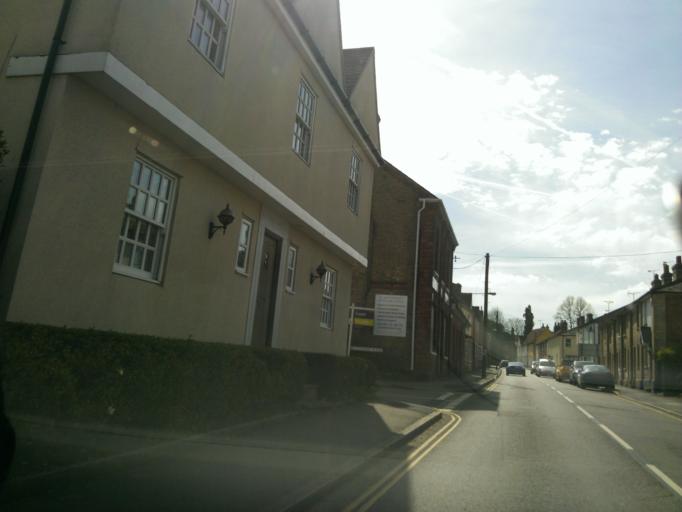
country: GB
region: England
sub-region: Essex
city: Kelvedon
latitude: 51.8400
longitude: 0.7052
